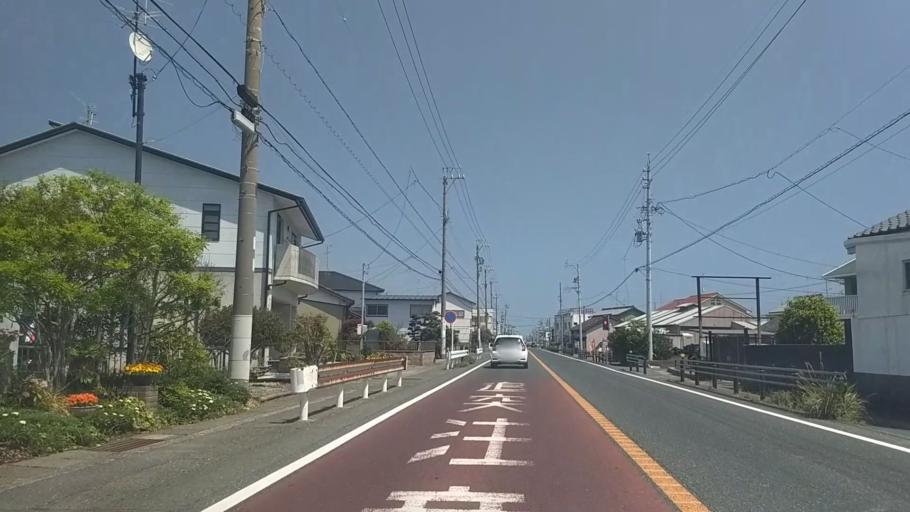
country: JP
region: Shizuoka
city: Kosai-shi
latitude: 34.6849
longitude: 137.6158
